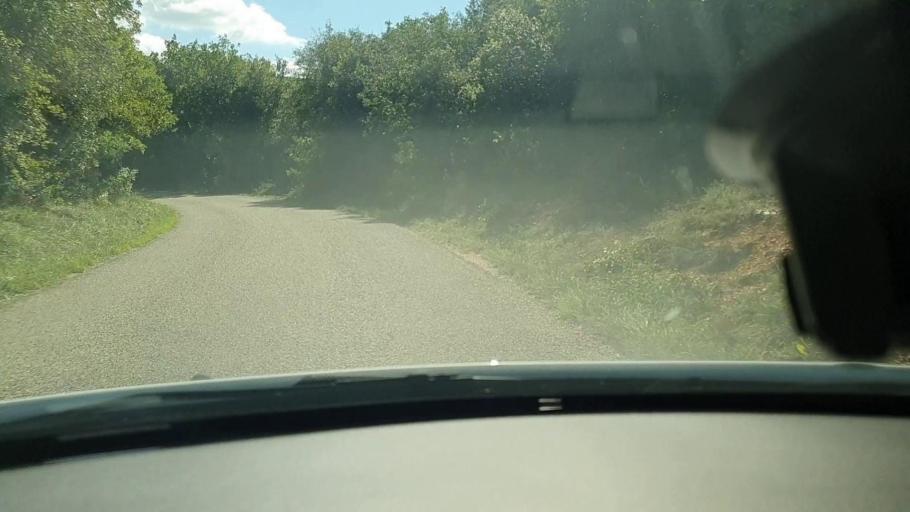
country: FR
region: Languedoc-Roussillon
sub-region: Departement du Gard
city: Goudargues
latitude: 44.1567
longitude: 4.4209
